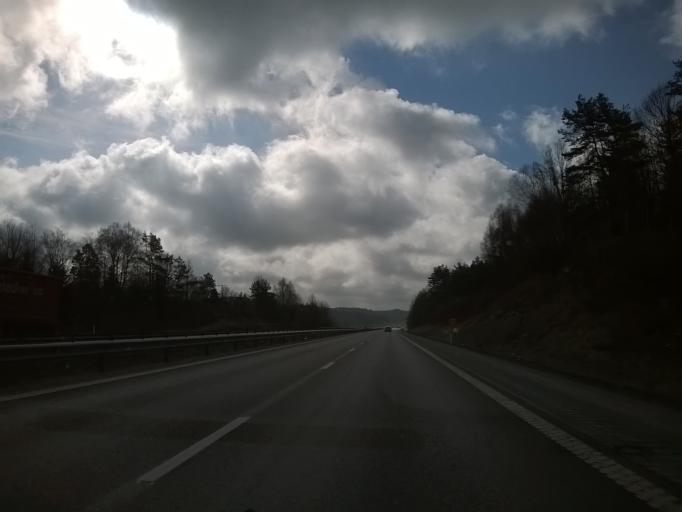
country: SE
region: Halland
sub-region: Kungsbacka Kommun
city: Frillesas
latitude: 57.3772
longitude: 12.1974
